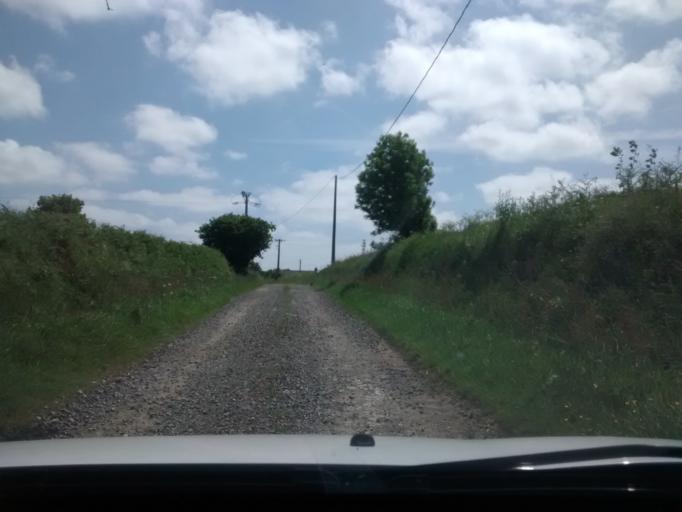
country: FR
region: Brittany
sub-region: Departement des Cotes-d'Armor
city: Louannec
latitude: 48.7816
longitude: -3.4080
